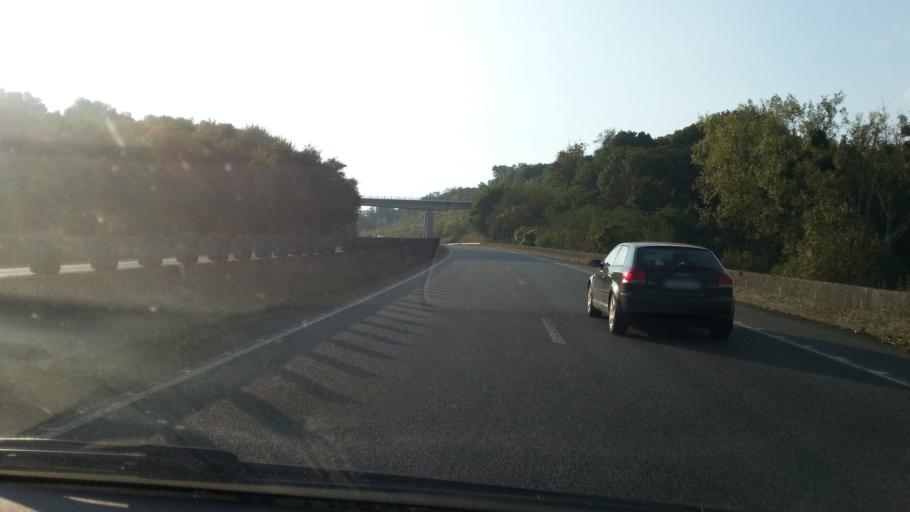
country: FR
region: Picardie
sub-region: Departement de l'Oise
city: Cambronne-les-Ribecourt
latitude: 49.5190
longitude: 2.9081
